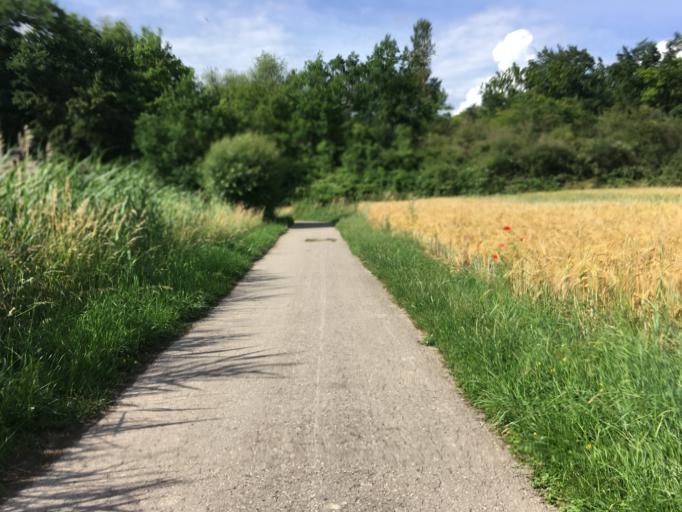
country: DE
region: Baden-Wuerttemberg
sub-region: Regierungsbezirk Stuttgart
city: Vaihingen an der Enz
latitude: 48.9572
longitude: 8.9672
